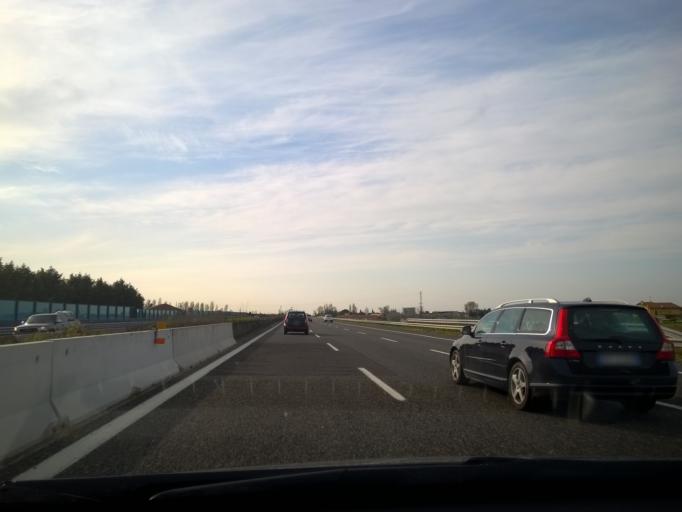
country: IT
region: Emilia-Romagna
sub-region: Forli-Cesena
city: San Mauro Pascoli
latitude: 44.1052
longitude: 12.4322
